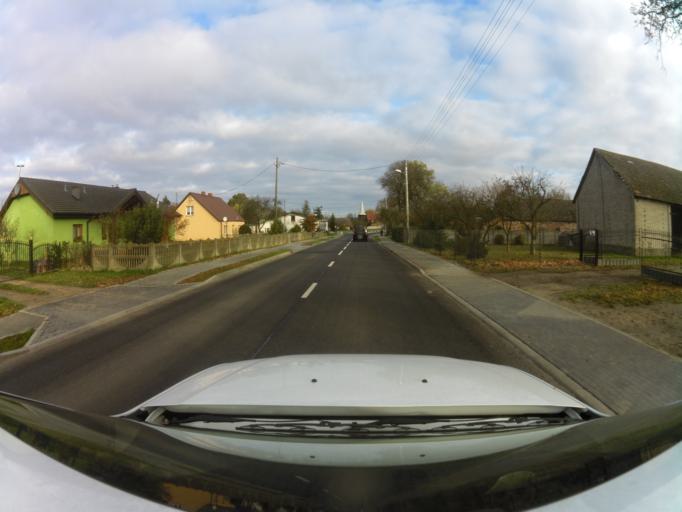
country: PL
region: West Pomeranian Voivodeship
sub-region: Powiat gryficki
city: Trzebiatow
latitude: 54.0097
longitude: 15.2444
